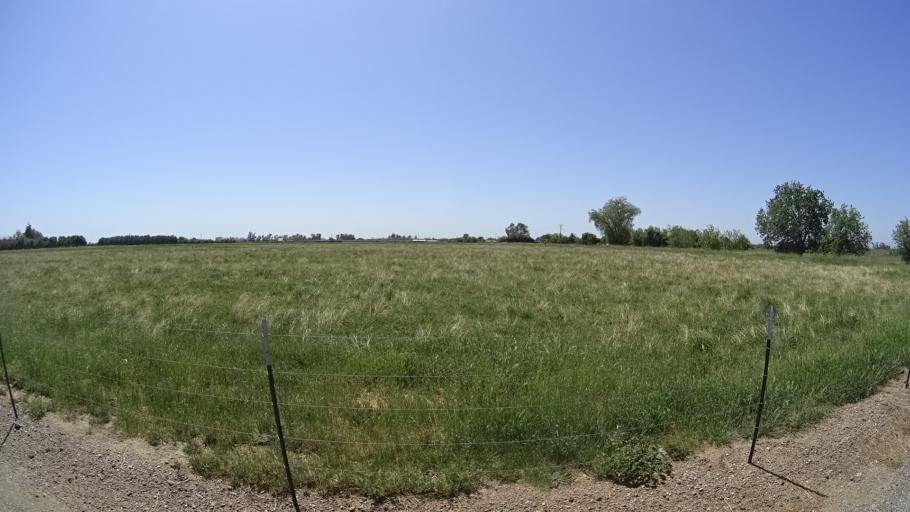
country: US
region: California
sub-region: Glenn County
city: Orland
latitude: 39.7835
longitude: -122.1828
